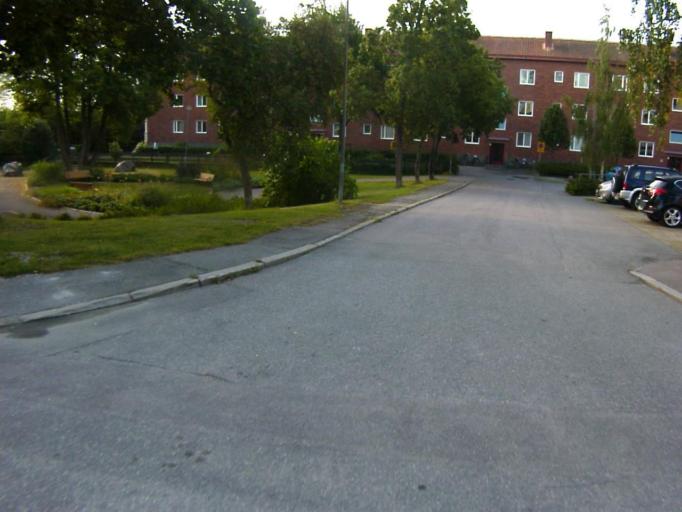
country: SE
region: Soedermanland
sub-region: Eskilstuna Kommun
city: Eskilstuna
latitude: 59.3746
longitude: 16.5352
